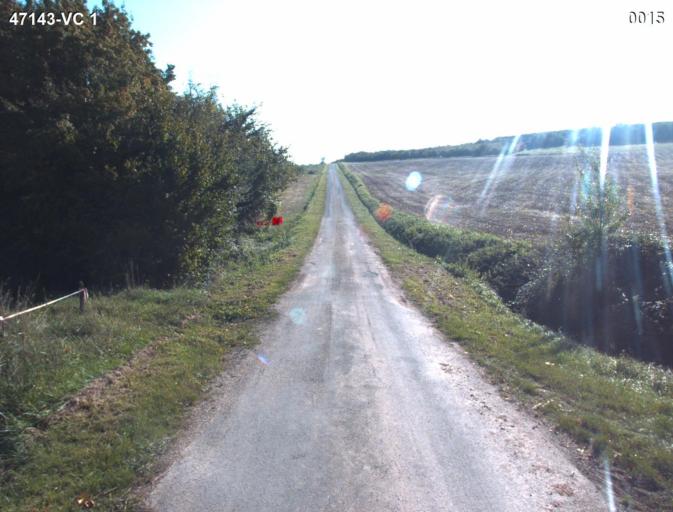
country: FR
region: Aquitaine
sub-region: Departement du Lot-et-Garonne
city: Vianne
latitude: 44.1931
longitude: 0.3405
